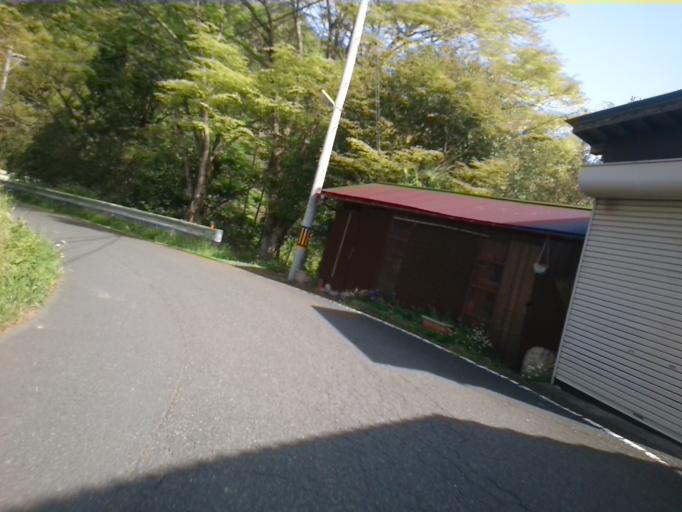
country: JP
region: Kyoto
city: Miyazu
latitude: 35.6332
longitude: 135.2311
